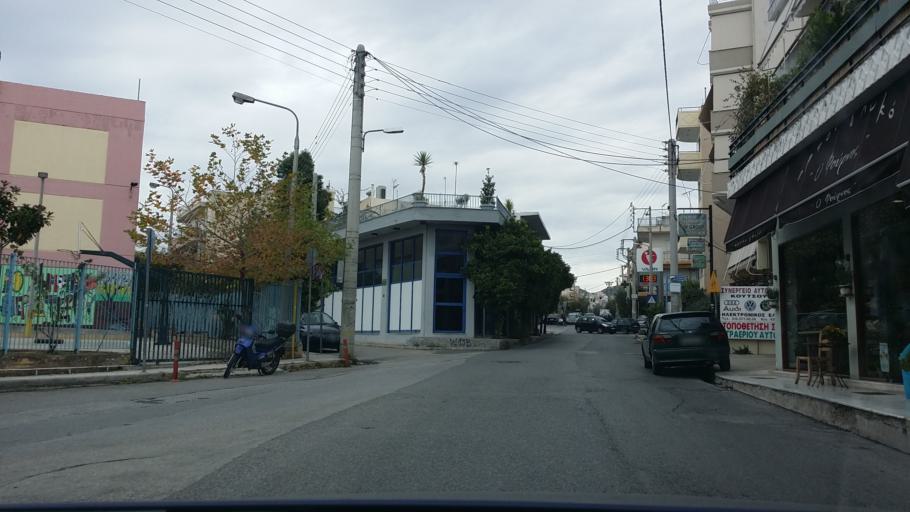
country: GR
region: Attica
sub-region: Nomarchia Athinas
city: Peristeri
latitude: 38.0270
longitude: 23.6893
